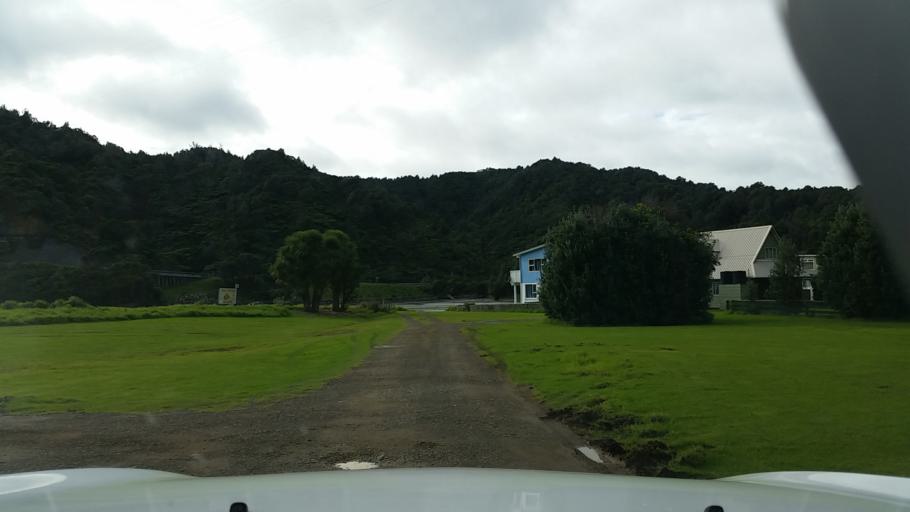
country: NZ
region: Taranaki
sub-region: New Plymouth District
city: Waitara
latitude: -38.8175
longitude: 174.5922
